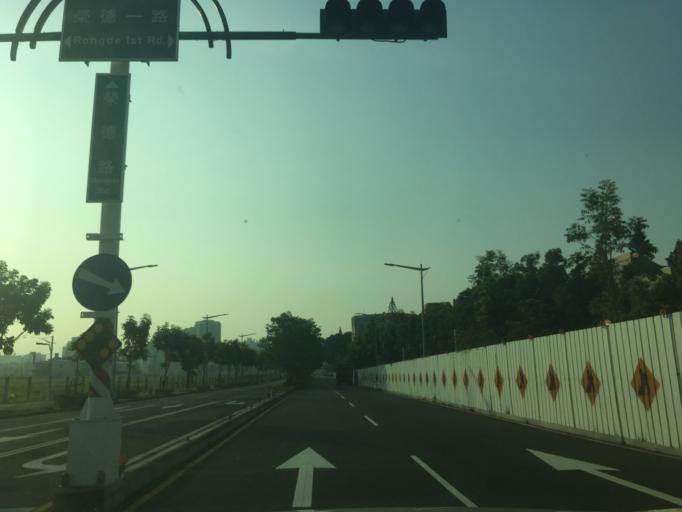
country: TW
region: Taiwan
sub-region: Taichung City
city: Taichung
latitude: 24.1864
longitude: 120.6737
